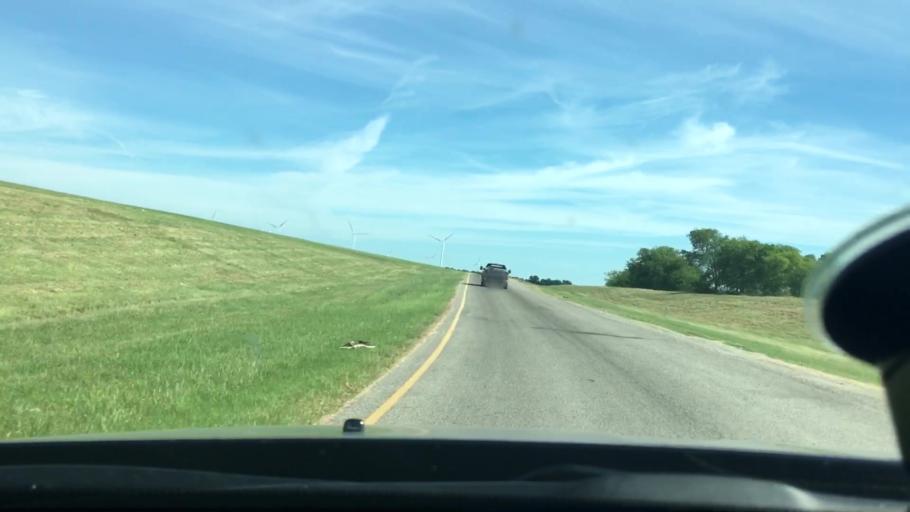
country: US
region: Oklahoma
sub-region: Carter County
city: Ardmore
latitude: 34.3333
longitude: -97.1511
